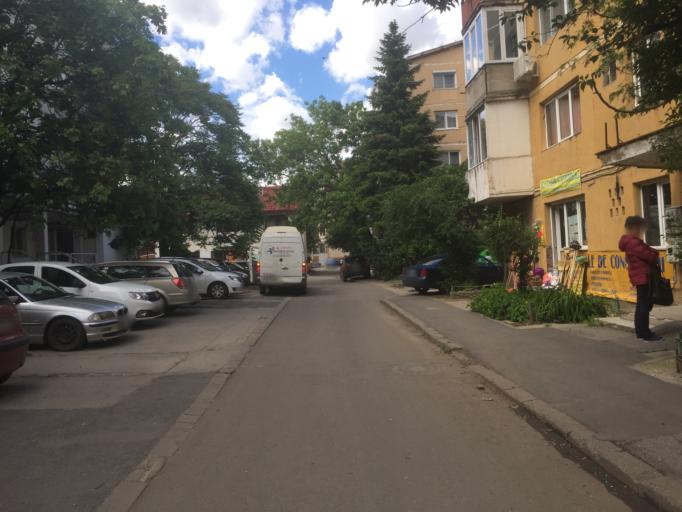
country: RO
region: Timis
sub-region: Comuna Giroc
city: Chisoda
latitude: 45.7305
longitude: 21.2107
